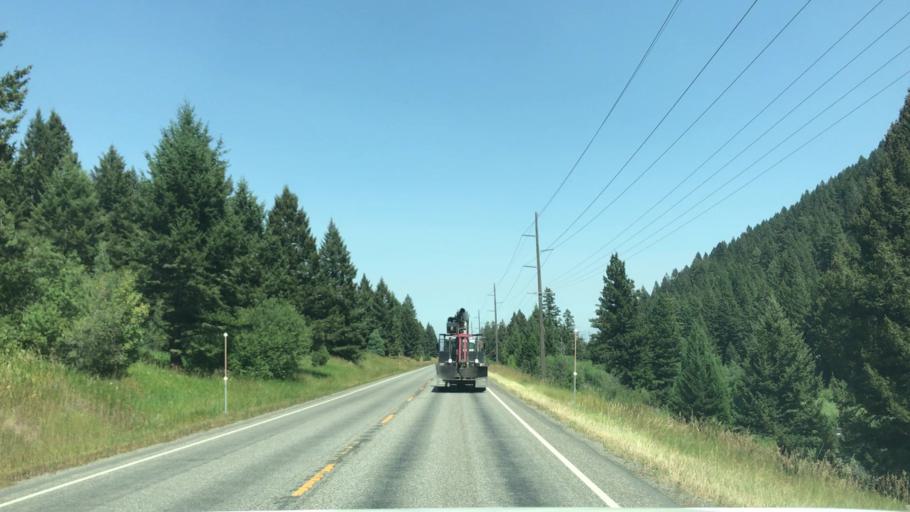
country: US
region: Montana
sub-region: Gallatin County
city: Four Corners
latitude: 45.5122
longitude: -111.2585
